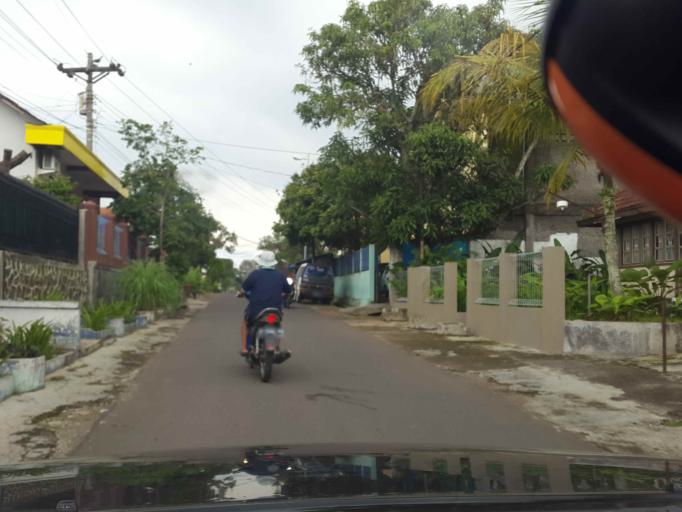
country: ID
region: Central Java
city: Salatiga
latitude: -7.3372
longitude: 110.5106
